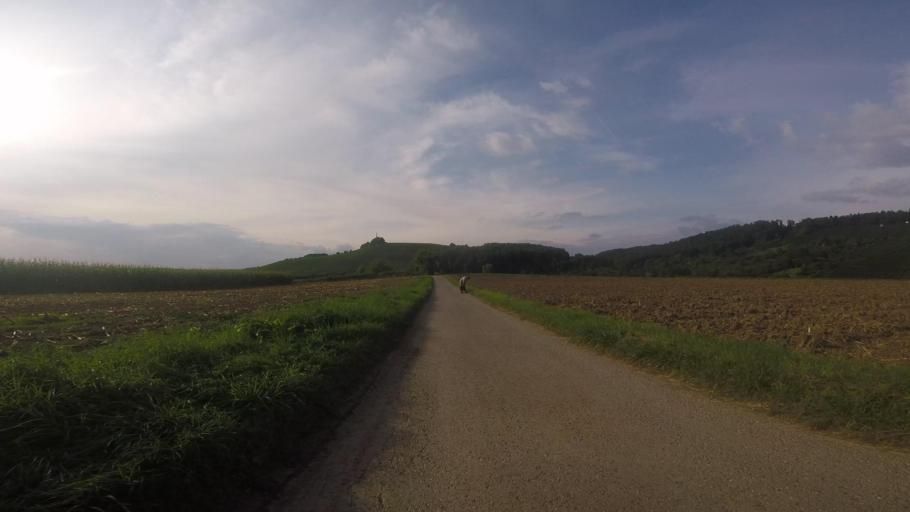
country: DE
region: Baden-Wuerttemberg
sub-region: Regierungsbezirk Stuttgart
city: Aspach
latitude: 48.9938
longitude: 9.3834
